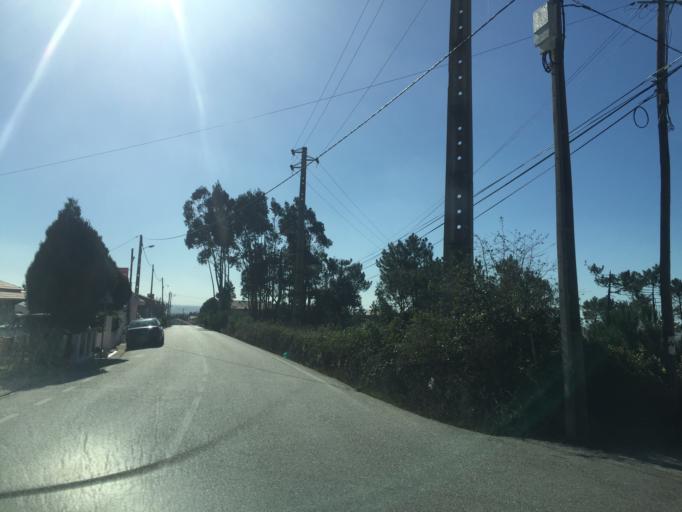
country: PT
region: Coimbra
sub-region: Figueira da Foz
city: Tavarede
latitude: 40.1841
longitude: -8.8382
